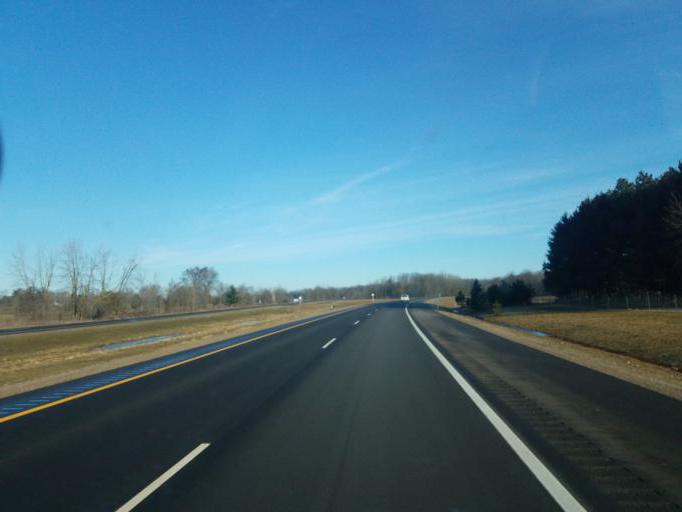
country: US
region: Michigan
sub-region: Gratiot County
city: Ithaca
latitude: 43.3067
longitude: -84.5968
